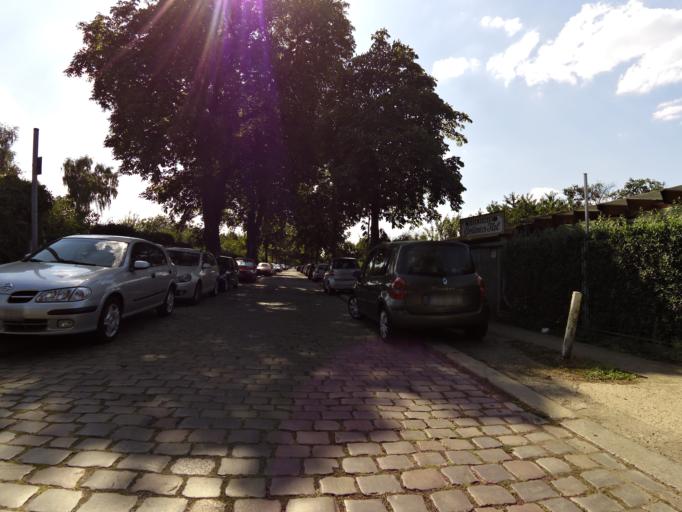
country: DE
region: Berlin
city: Schoneberg Bezirk
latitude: 52.4688
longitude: 13.3559
